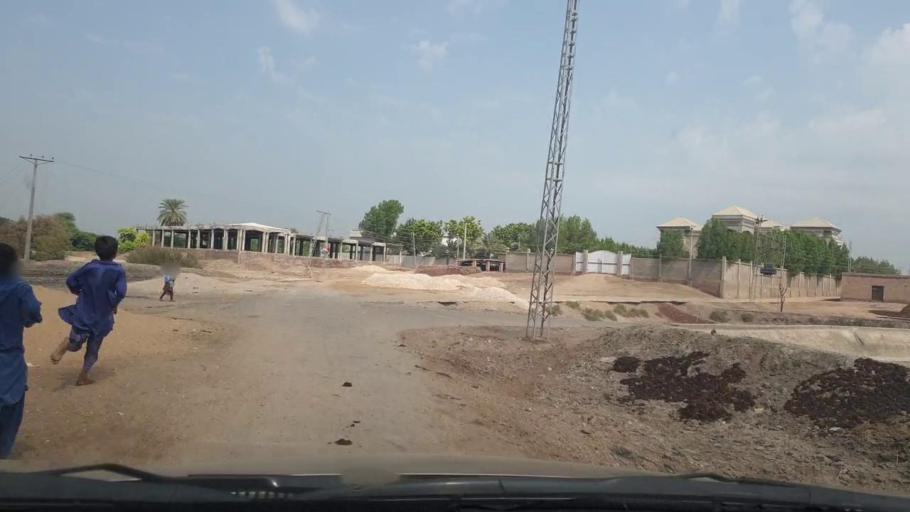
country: PK
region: Sindh
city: Larkana
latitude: 27.6642
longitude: 68.1818
